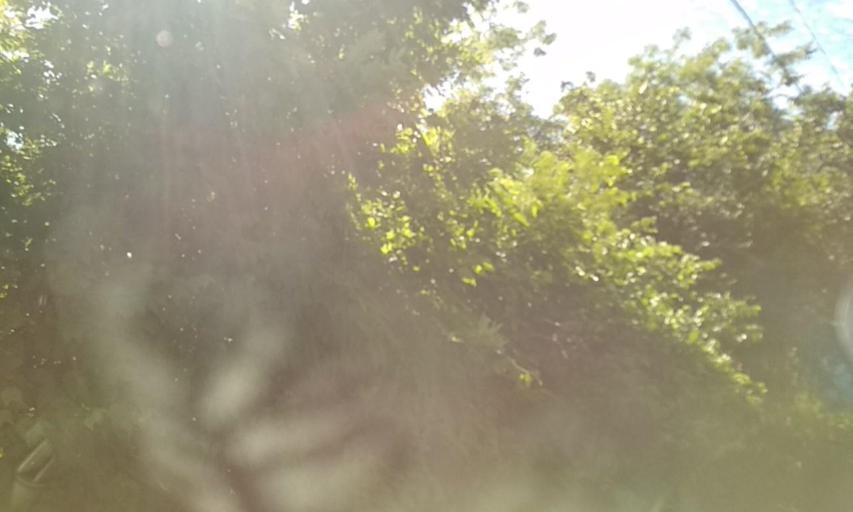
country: MX
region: Veracruz
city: Cazones de Herrera
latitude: 20.6447
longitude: -97.3042
